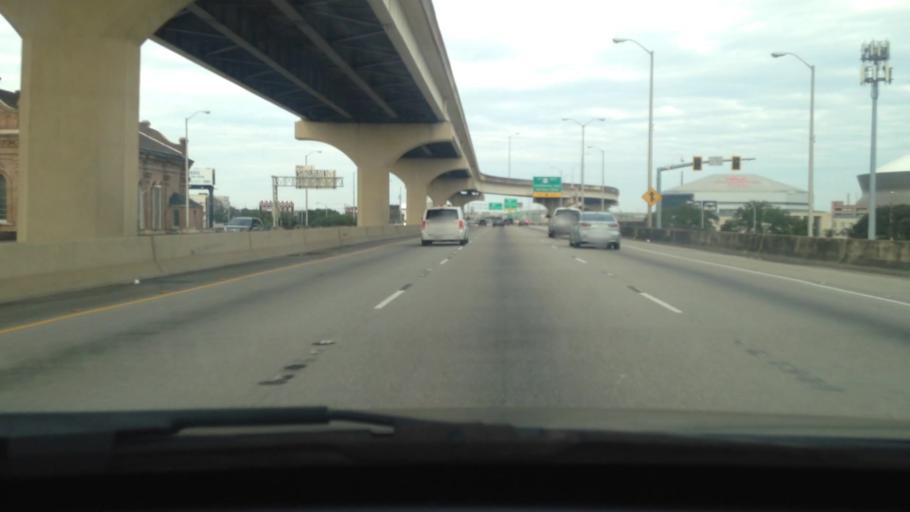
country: US
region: Louisiana
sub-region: Orleans Parish
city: New Orleans
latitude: 29.9439
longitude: -90.0762
